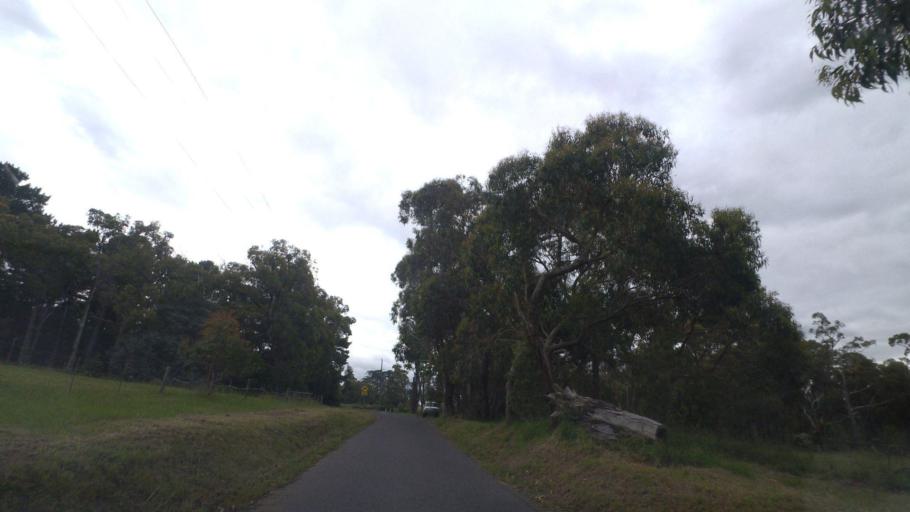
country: AU
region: Victoria
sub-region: Yarra Ranges
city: Mount Evelyn
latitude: -37.7668
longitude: 145.4188
